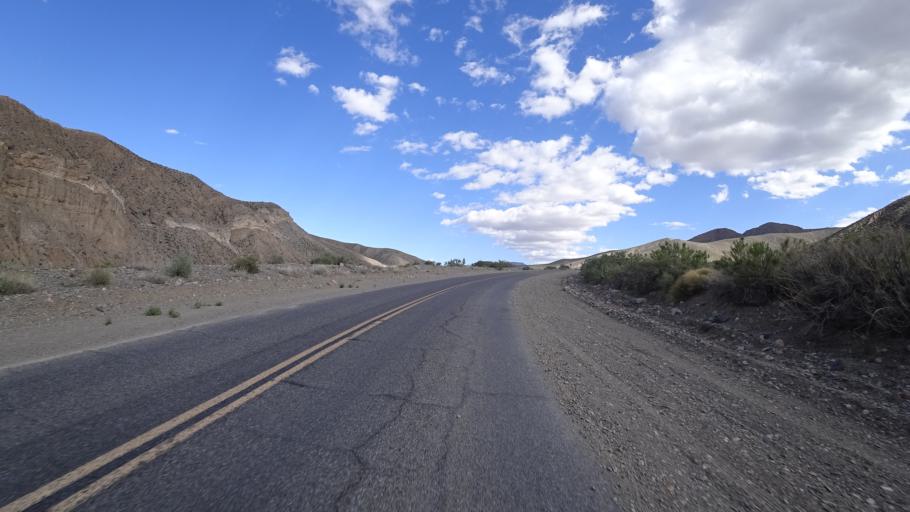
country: US
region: Nevada
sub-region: Nye County
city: Beatty
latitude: 36.4078
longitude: -117.1719
